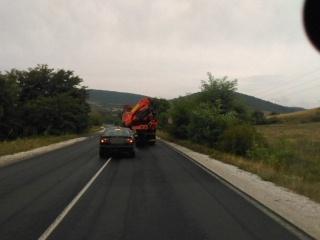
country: BG
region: Plovdiv
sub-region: Obshtina Karlovo
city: Karlovo
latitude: 42.5295
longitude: 24.8167
